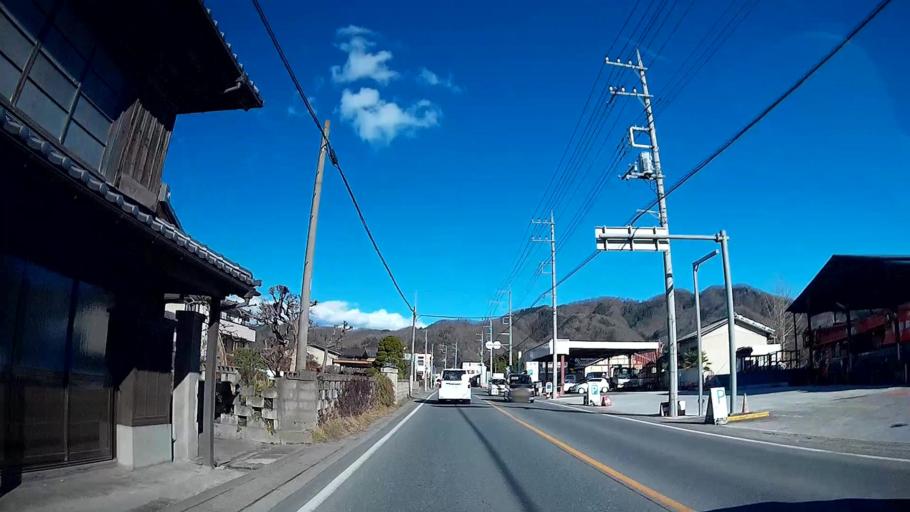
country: JP
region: Saitama
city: Yorii
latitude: 36.0838
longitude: 139.1108
